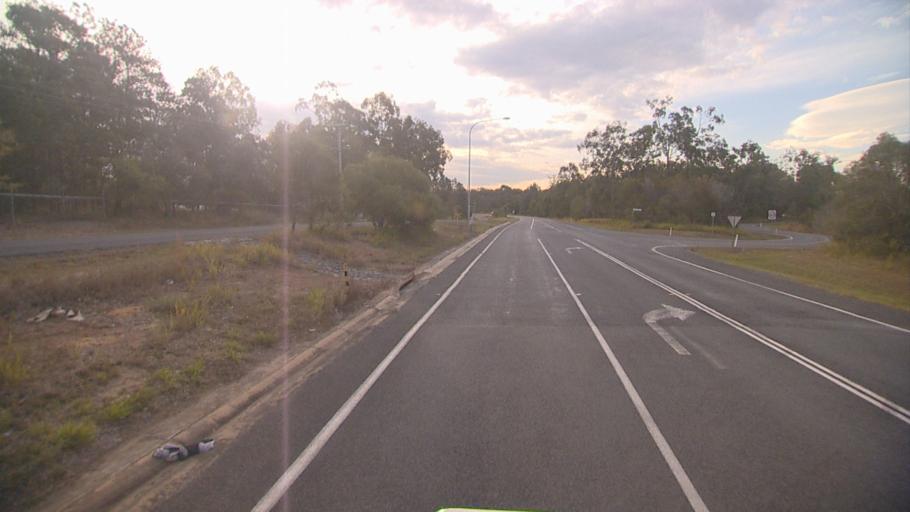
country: AU
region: Queensland
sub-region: Logan
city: Cedar Vale
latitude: -27.8451
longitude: 153.1191
